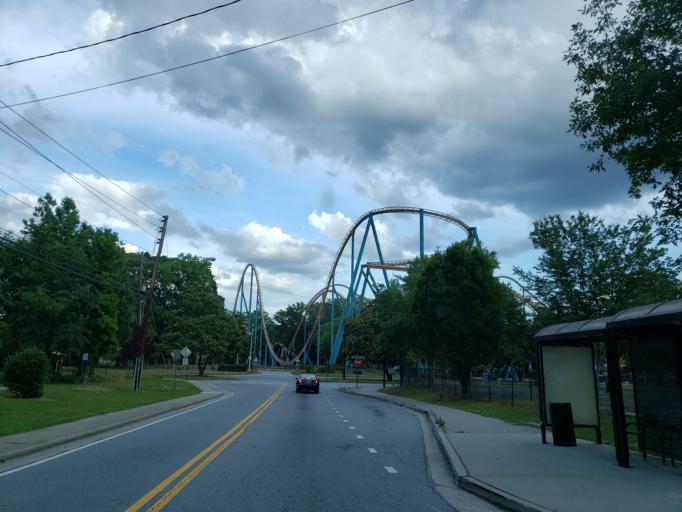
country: US
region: Georgia
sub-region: Cobb County
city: Mableton
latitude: 33.7718
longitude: -84.5531
